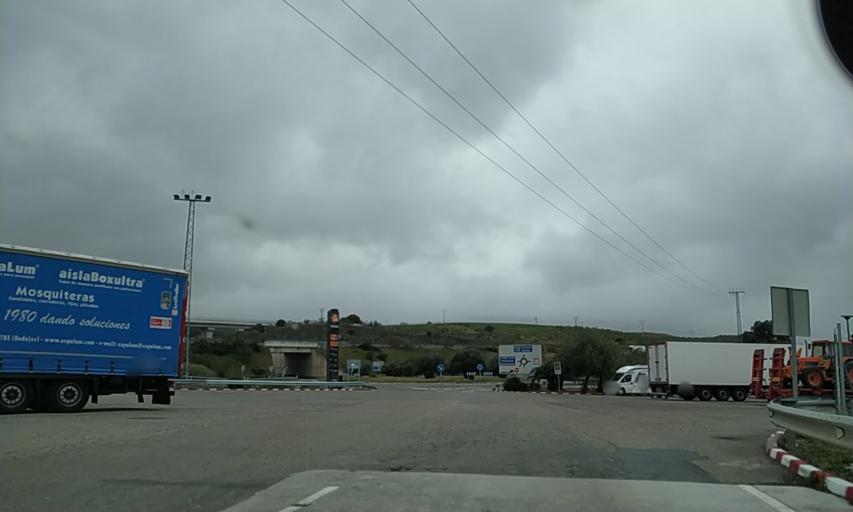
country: ES
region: Extremadura
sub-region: Provincia de Caceres
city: Riolobos
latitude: 39.8833
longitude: -6.2766
